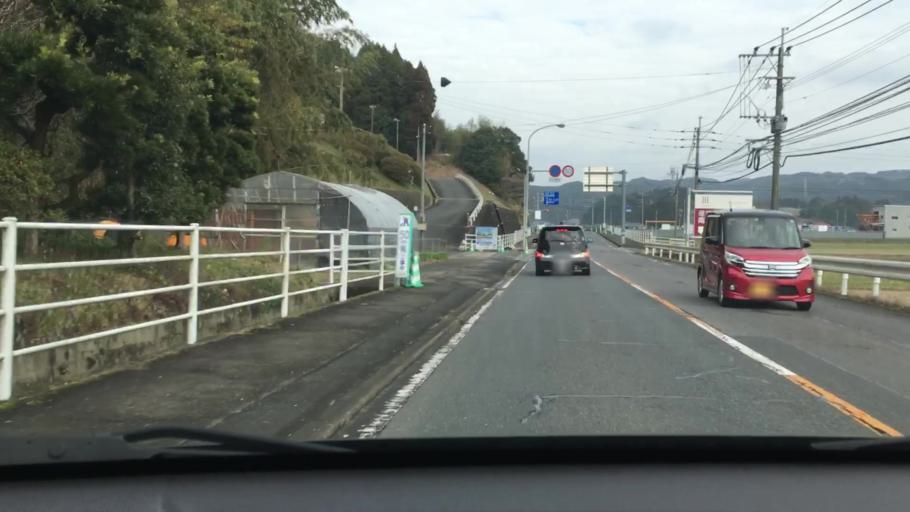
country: JP
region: Saga Prefecture
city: Imaricho-ko
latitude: 33.3051
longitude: 129.9240
